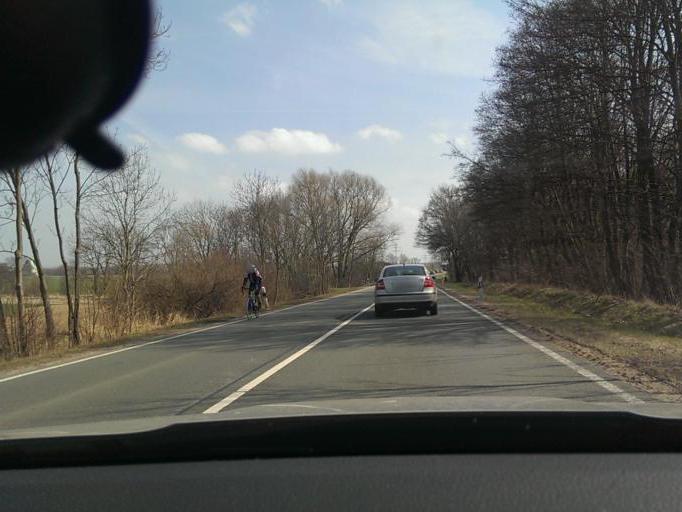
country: DE
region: Thuringia
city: Hohenkirchen
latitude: 50.8422
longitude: 10.7151
